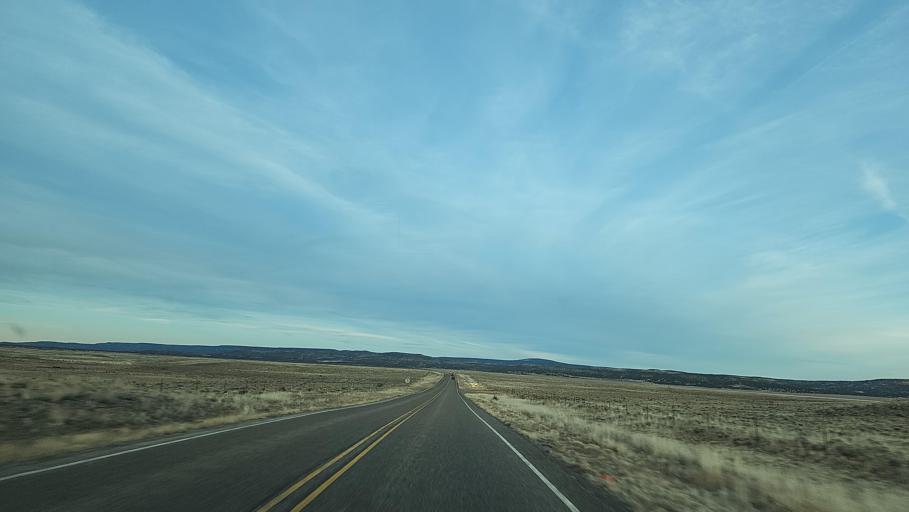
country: US
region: New Mexico
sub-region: Cibola County
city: Grants
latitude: 34.6977
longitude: -108.0469
